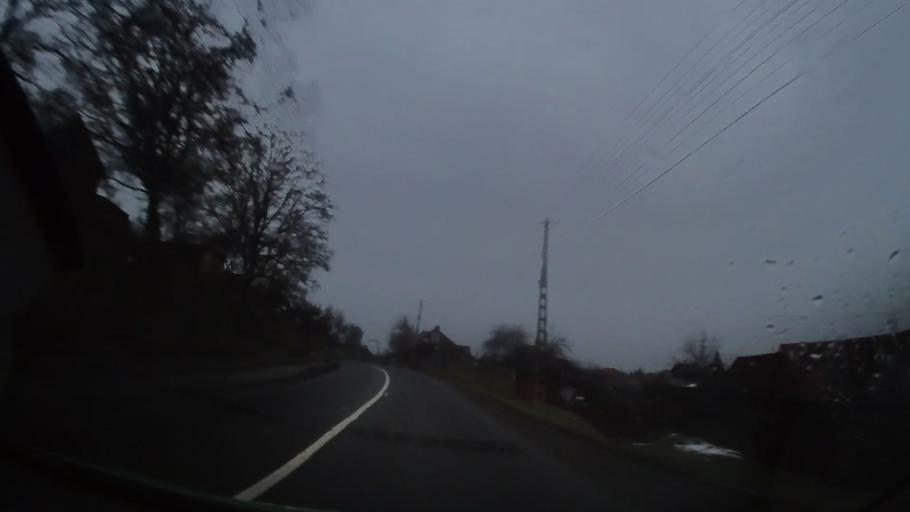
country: RO
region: Harghita
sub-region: Comuna Remetea
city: Remetea
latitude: 46.7965
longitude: 25.4567
